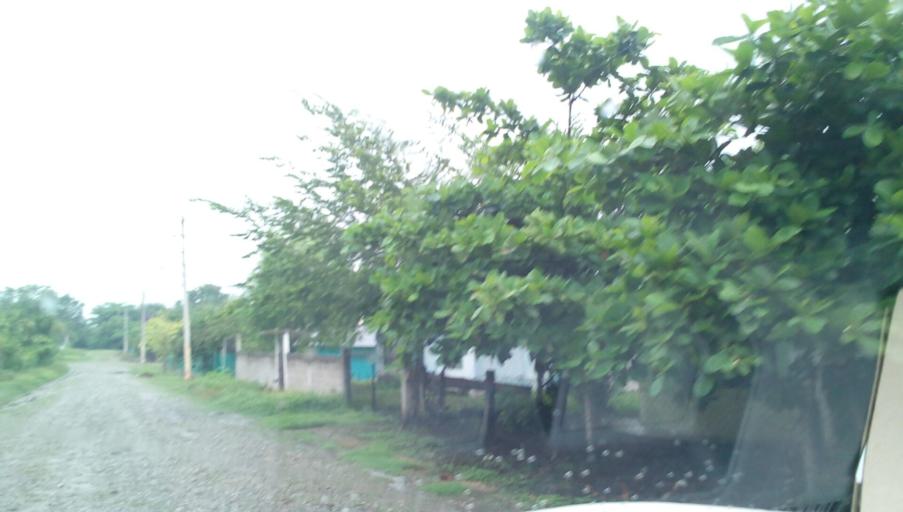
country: MX
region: Veracruz
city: Tempoal de Sanchez
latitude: 21.4196
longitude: -98.4261
